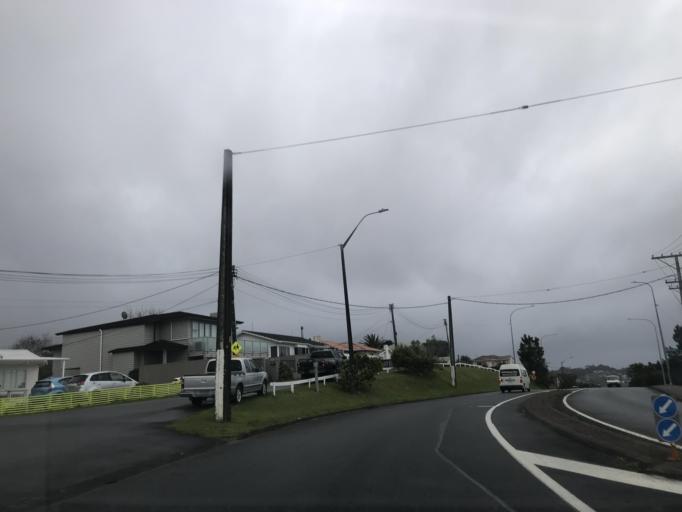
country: NZ
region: Auckland
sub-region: Auckland
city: Rothesay Bay
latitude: -36.7265
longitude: 174.7244
